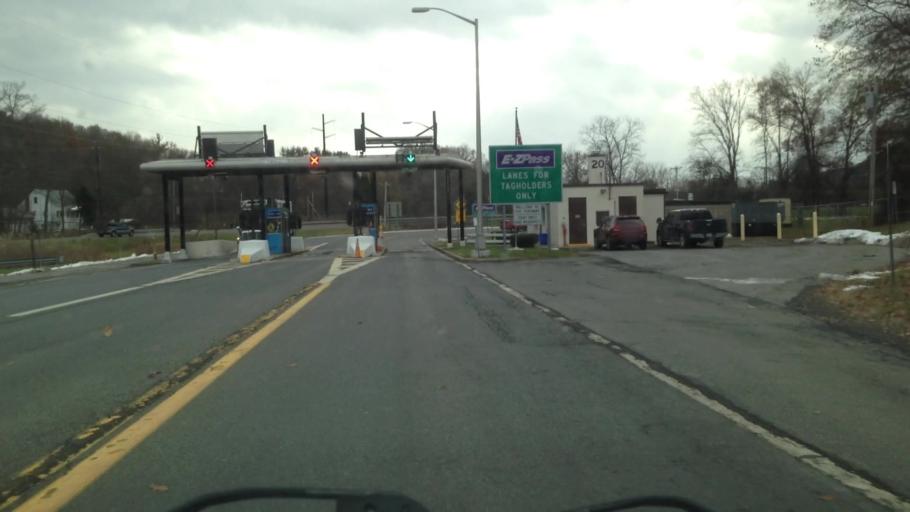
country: US
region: New York
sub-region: Ulster County
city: Saugerties
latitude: 42.0828
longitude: -73.9711
